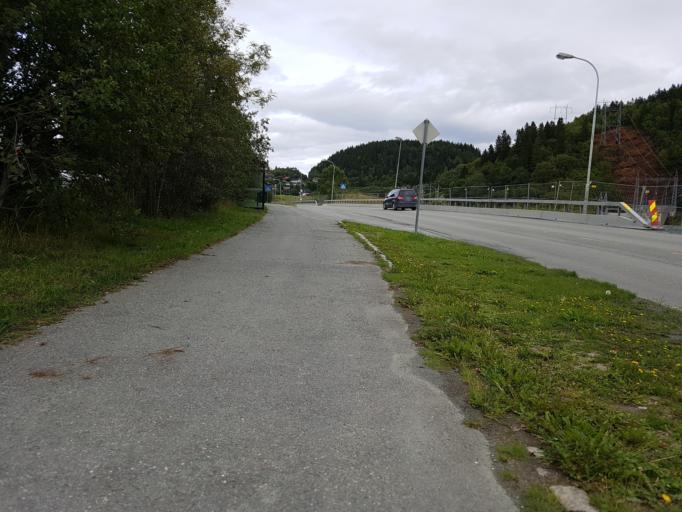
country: NO
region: Sor-Trondelag
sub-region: Trondheim
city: Trondheim
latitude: 63.3916
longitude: 10.4356
